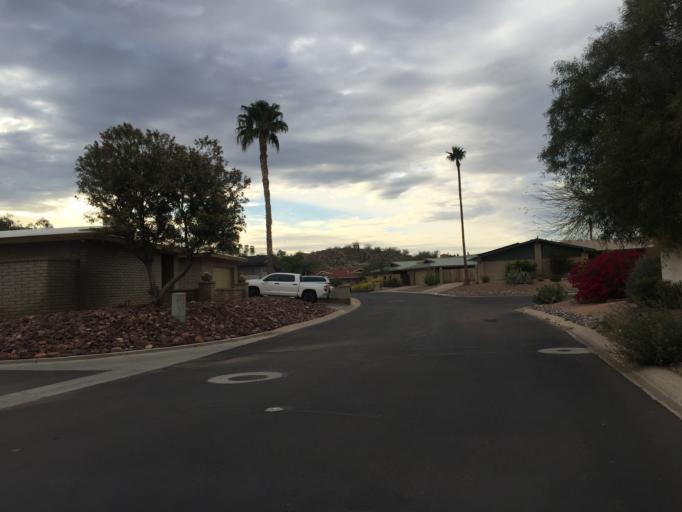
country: US
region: Arizona
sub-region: Maricopa County
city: Paradise Valley
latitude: 33.5726
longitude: -112.0143
